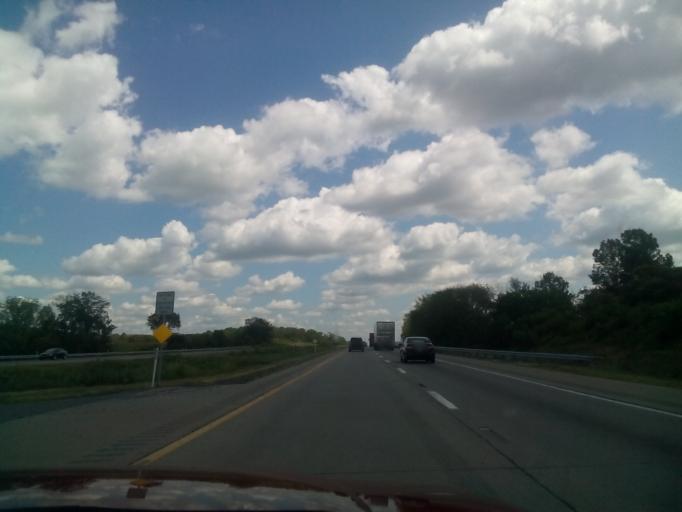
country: US
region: Pennsylvania
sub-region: Northumberland County
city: Riverside
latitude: 40.9869
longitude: -76.7053
